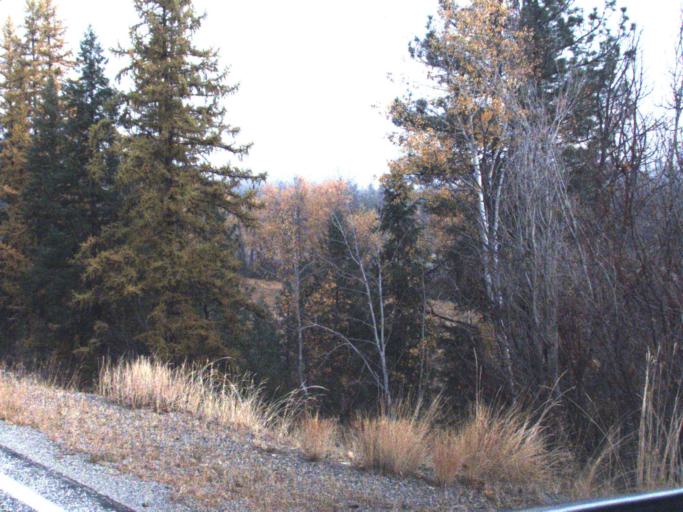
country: CA
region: British Columbia
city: Grand Forks
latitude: 48.8729
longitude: -118.2132
